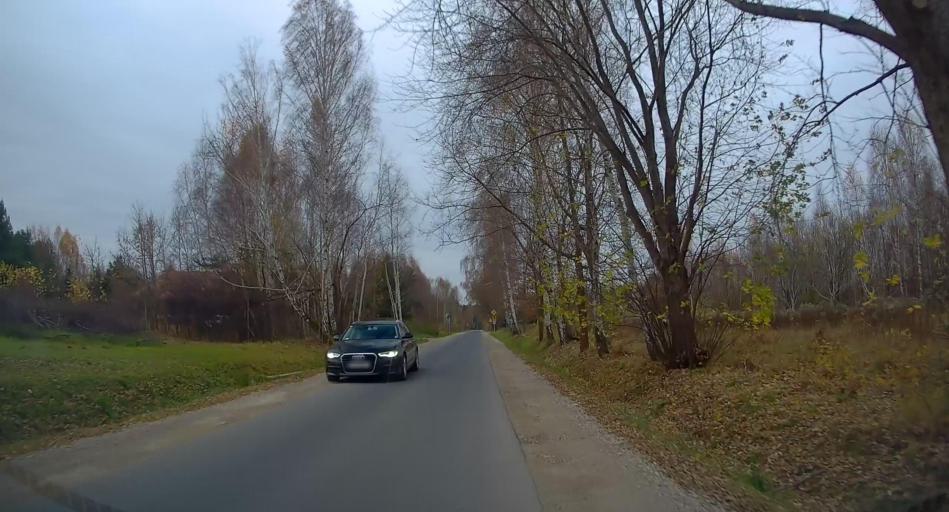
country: PL
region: Lodz Voivodeship
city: Zabia Wola
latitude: 52.0143
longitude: 20.6554
